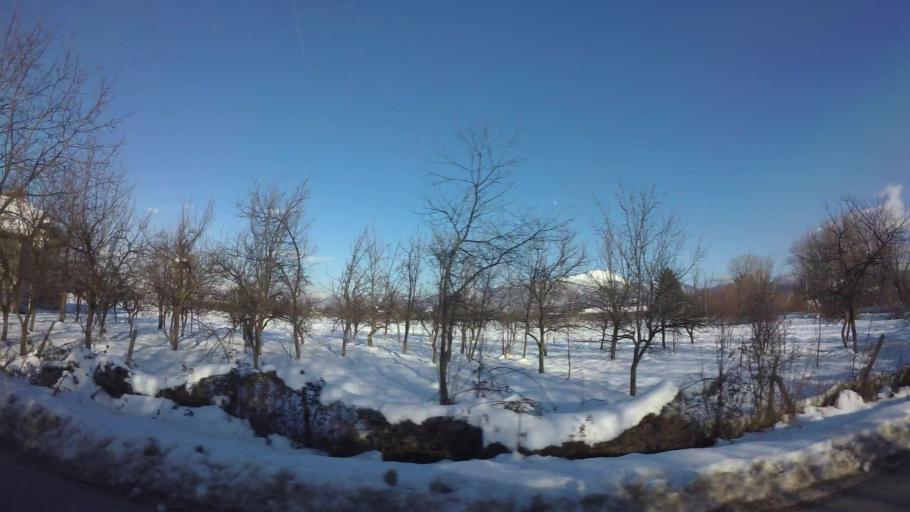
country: BA
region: Federation of Bosnia and Herzegovina
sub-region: Kanton Sarajevo
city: Sarajevo
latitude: 43.8165
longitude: 18.3440
